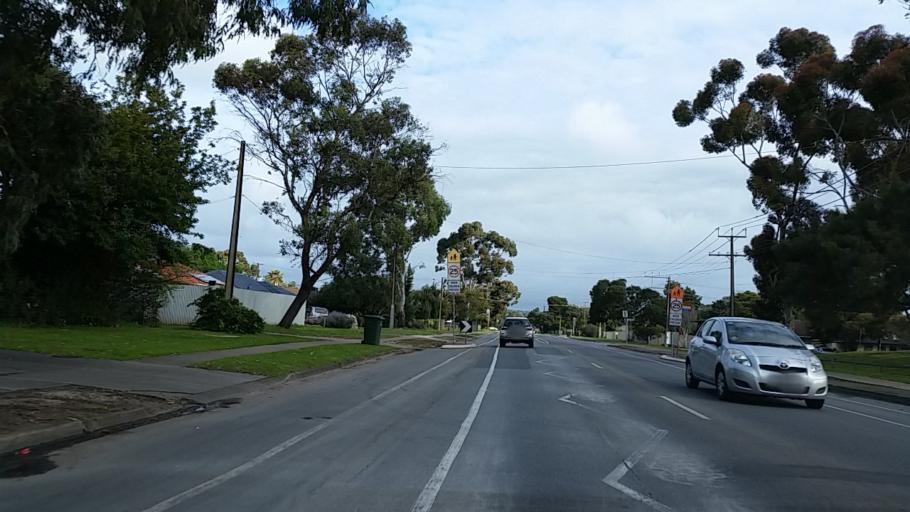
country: AU
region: South Australia
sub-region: Onkaparinga
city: Morphett Vale
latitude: -35.1278
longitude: 138.5365
